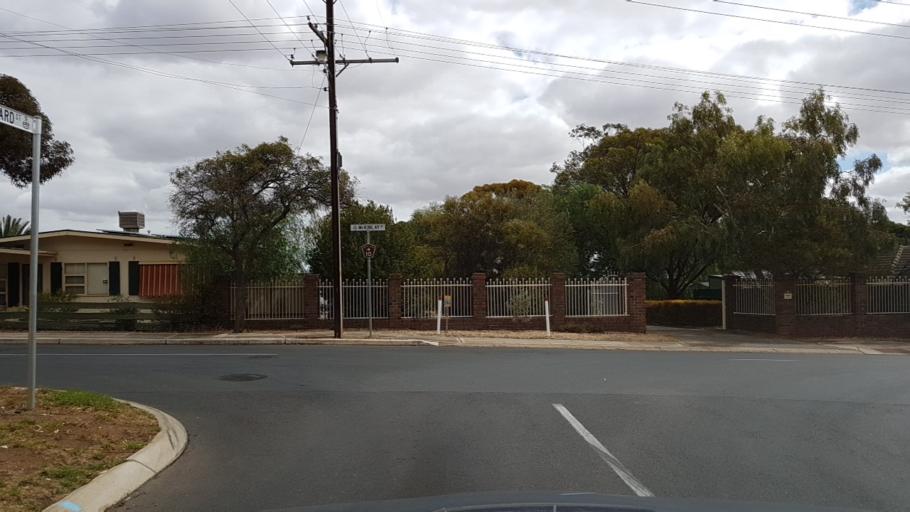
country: AU
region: South Australia
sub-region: Gawler
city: Gawler
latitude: -34.6044
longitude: 138.7543
